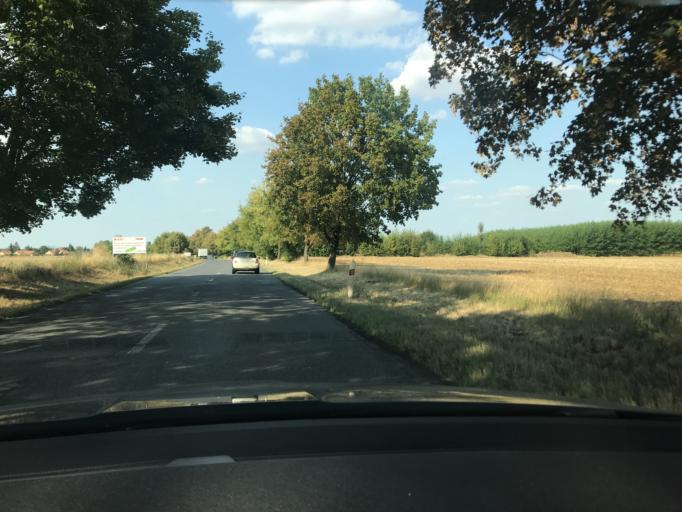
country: CZ
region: Central Bohemia
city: Velke Prilepy
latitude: 50.1808
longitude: 14.3201
